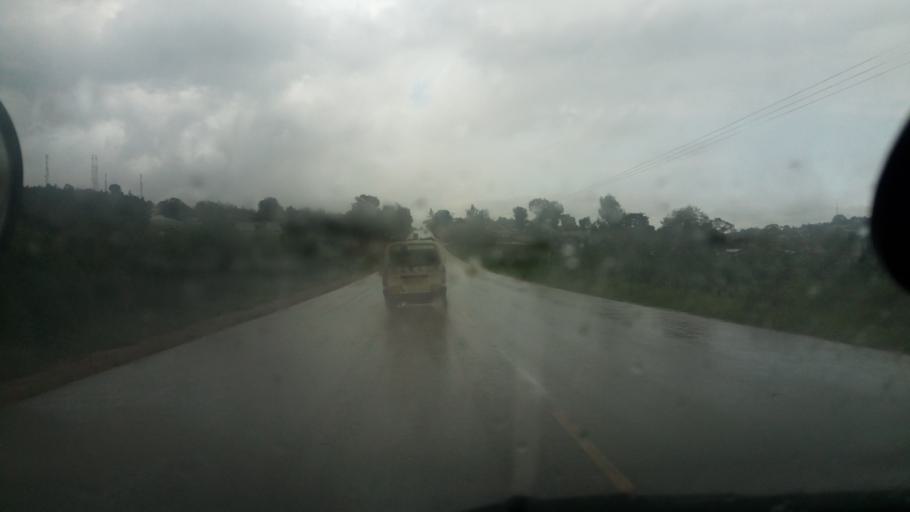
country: UG
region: Central Region
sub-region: Wakiso District
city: Wakiso
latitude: 0.4069
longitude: 32.4691
